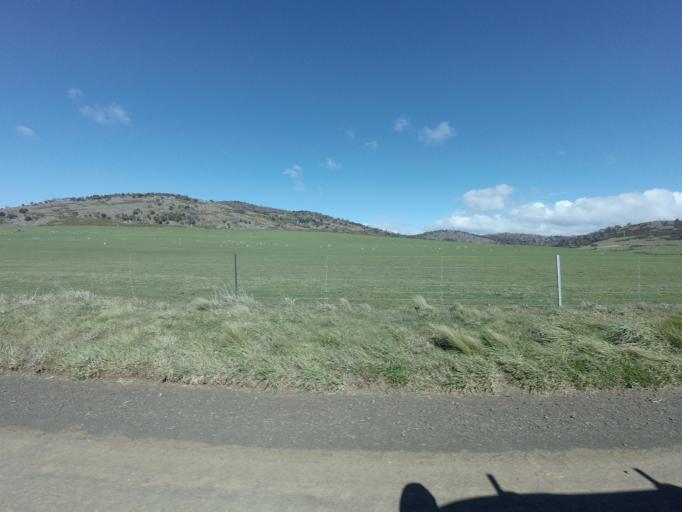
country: AU
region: Tasmania
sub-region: Northern Midlands
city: Evandale
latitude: -41.9181
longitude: 147.3914
